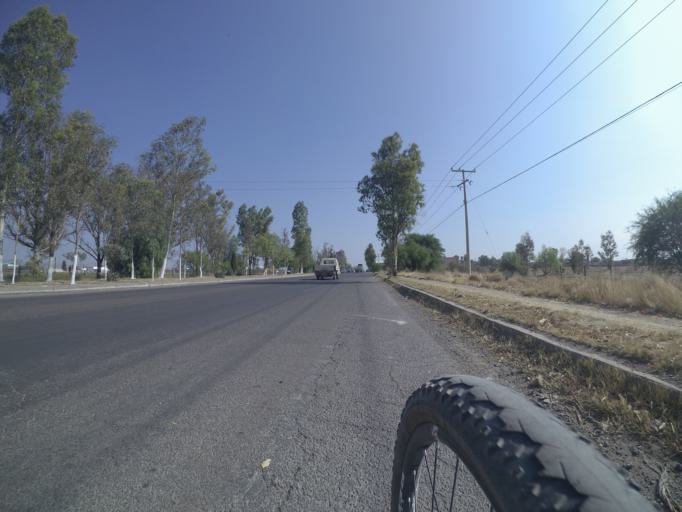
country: MX
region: Aguascalientes
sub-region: Jesus Maria
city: Paseos de las Haciendas [Fraccionamiento]
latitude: 21.9797
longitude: -102.3377
